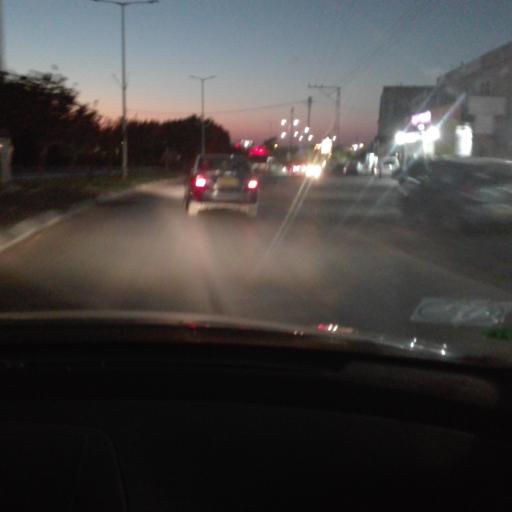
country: PS
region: West Bank
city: Nazlat `Isa
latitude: 32.4275
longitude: 35.0317
